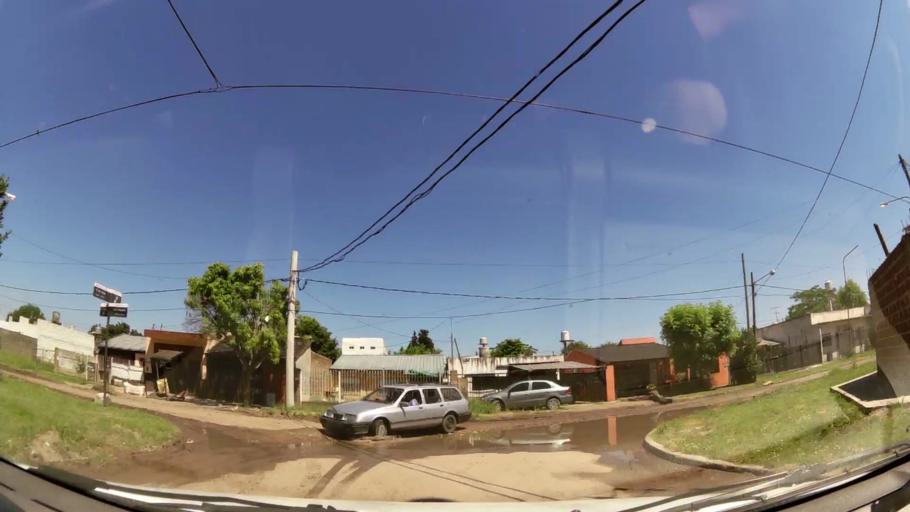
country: AR
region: Buenos Aires
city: Ituzaingo
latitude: -34.6851
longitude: -58.6671
